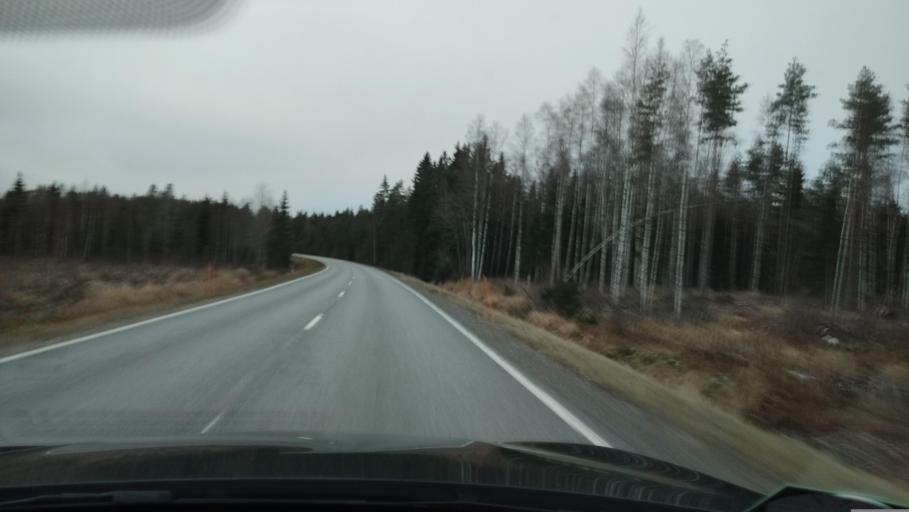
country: FI
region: Southern Ostrobothnia
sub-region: Suupohja
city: Karijoki
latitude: 62.3283
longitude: 21.8496
